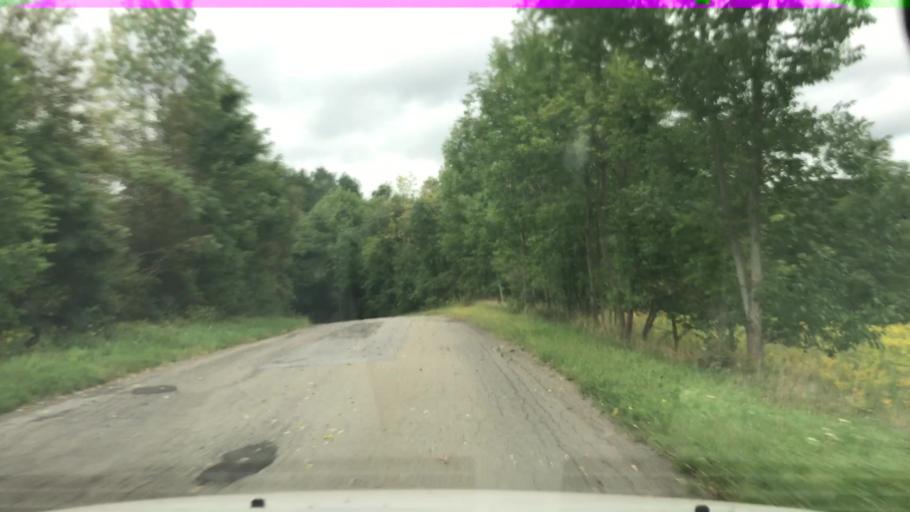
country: US
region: New York
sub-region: Cattaraugus County
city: Little Valley
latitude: 42.3224
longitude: -78.7245
